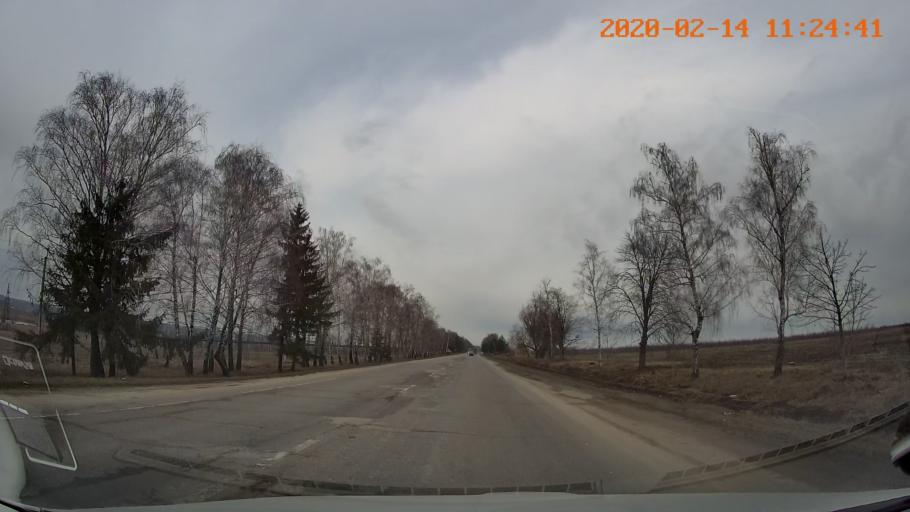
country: MD
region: Briceni
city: Briceni
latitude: 48.3408
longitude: 27.1127
